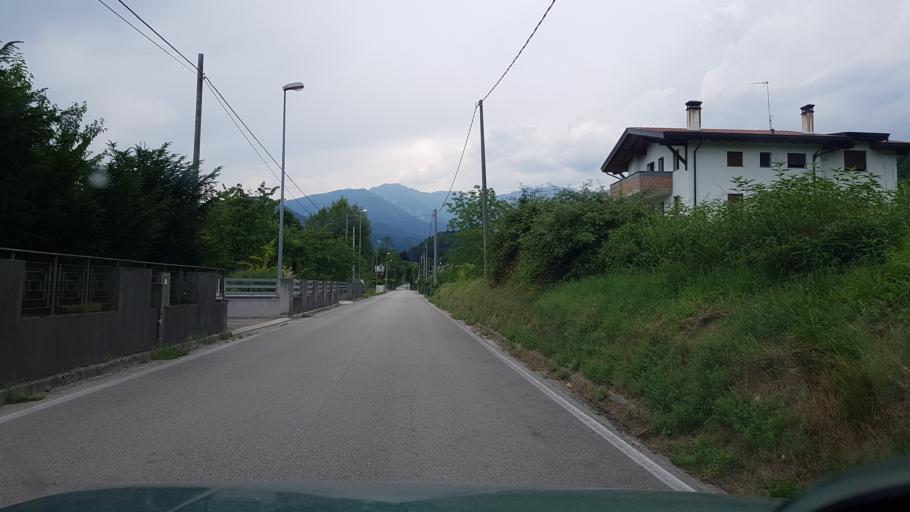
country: IT
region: Friuli Venezia Giulia
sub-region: Provincia di Udine
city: Tarcento
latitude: 46.2109
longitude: 13.2285
